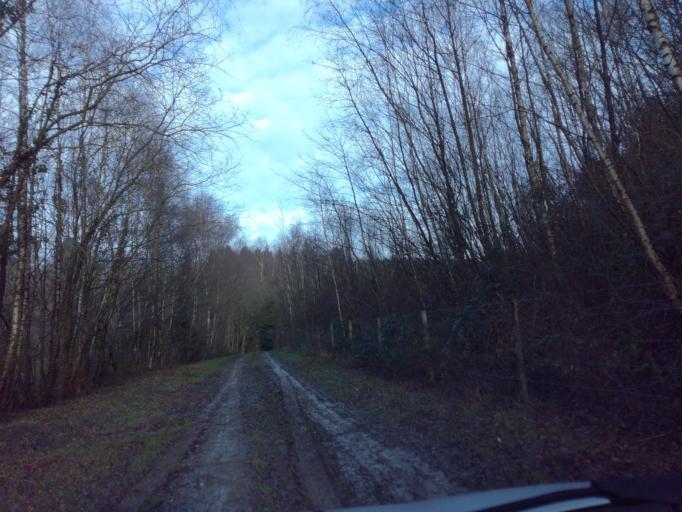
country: FR
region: Brittany
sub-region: Departement d'Ille-et-Vilaine
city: Liffre
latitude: 48.1958
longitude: -1.4792
